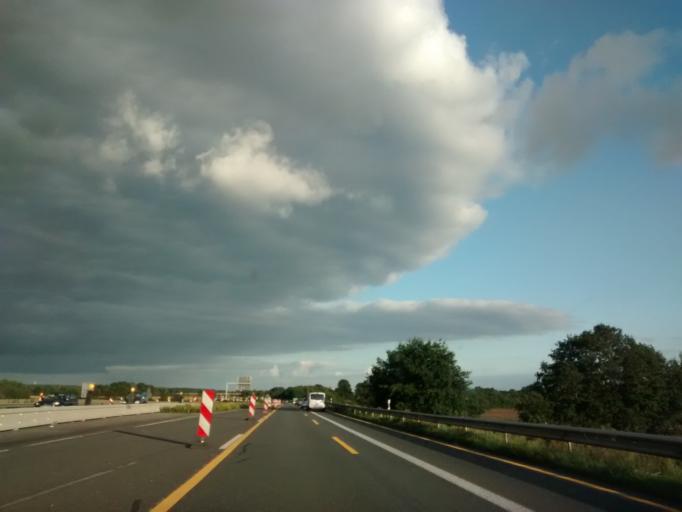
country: DE
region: Lower Saxony
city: Salzbergen
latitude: 52.3382
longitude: 7.2920
